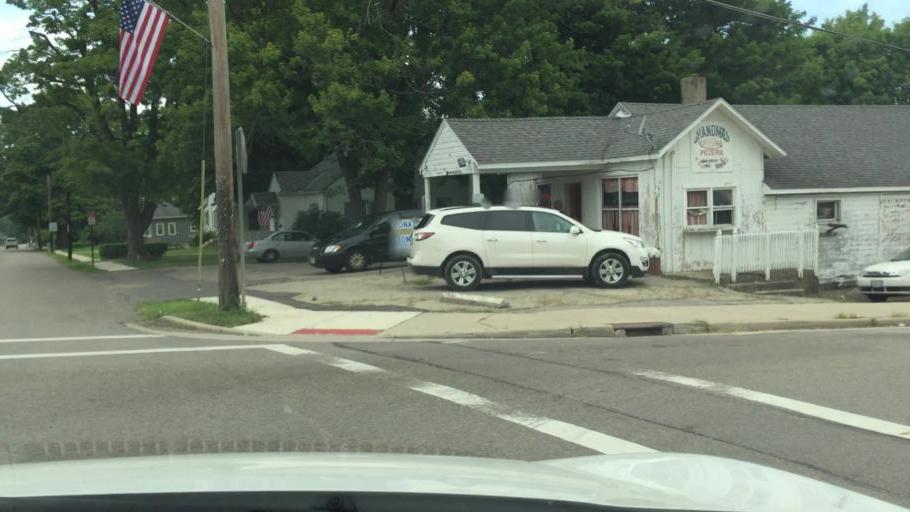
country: US
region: Ohio
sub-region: Champaign County
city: Mechanicsburg
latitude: 40.0752
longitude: -83.5630
